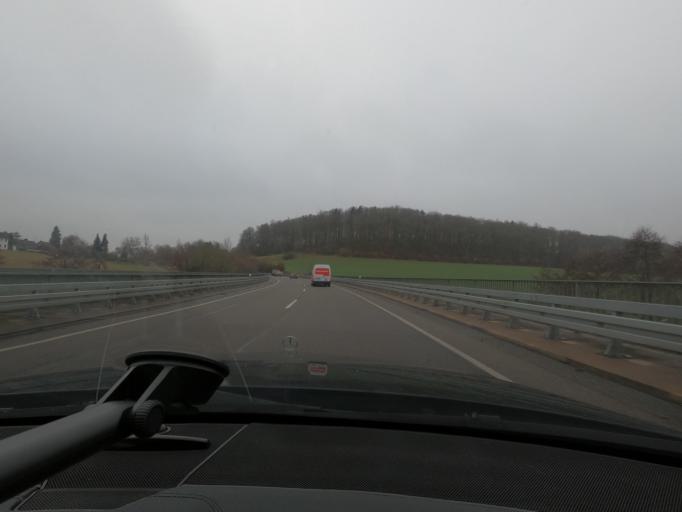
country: DE
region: Hesse
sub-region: Regierungsbezirk Kassel
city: Bad Arolsen
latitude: 51.3870
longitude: 8.9946
